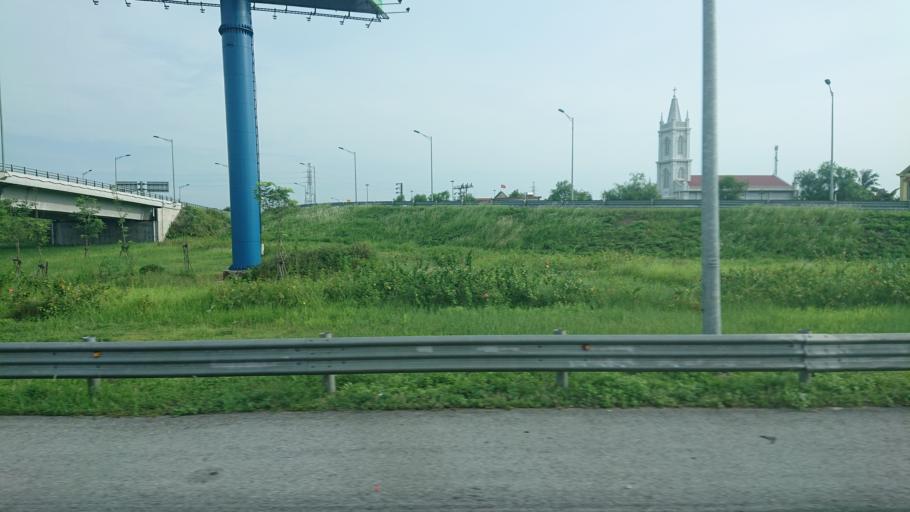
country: VN
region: Hai Phong
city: An Lao
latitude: 20.8034
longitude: 106.5245
